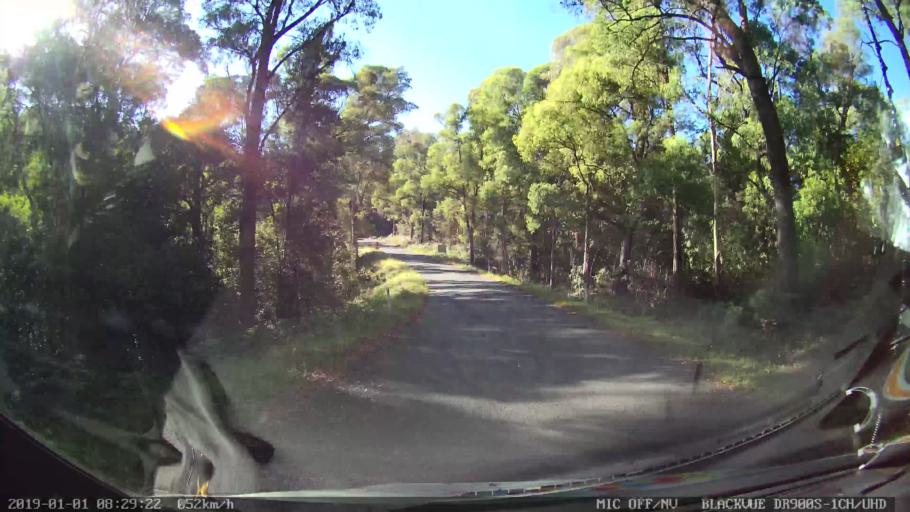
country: AU
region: New South Wales
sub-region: Snowy River
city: Jindabyne
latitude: -36.3751
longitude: 148.1927
